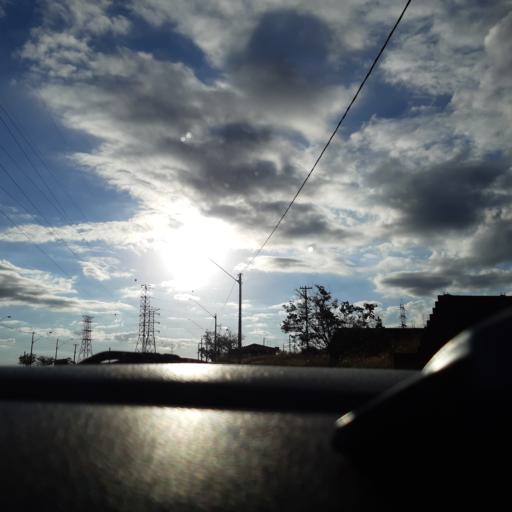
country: BR
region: Sao Paulo
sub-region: Ourinhos
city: Ourinhos
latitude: -22.9979
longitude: -49.8508
